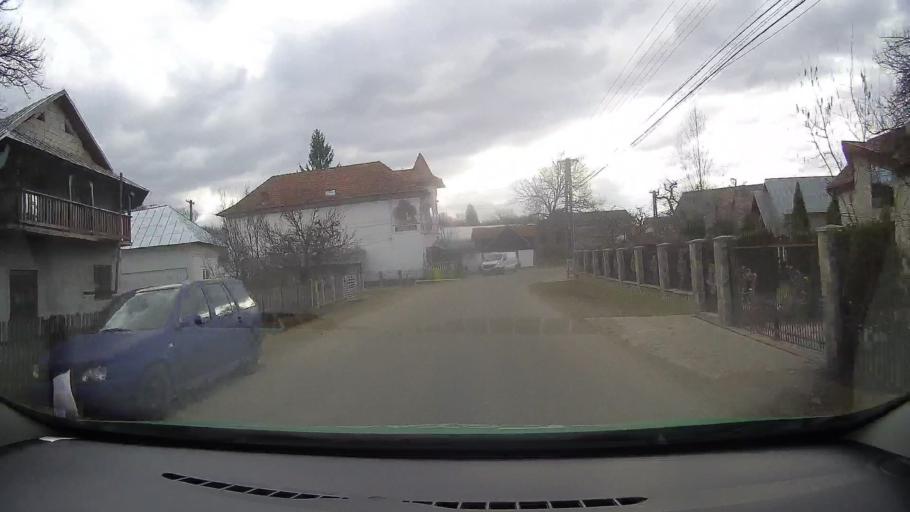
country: RO
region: Dambovita
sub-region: Comuna Valea Lunga
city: Valea Lunga-Cricov
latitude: 45.0763
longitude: 25.5759
